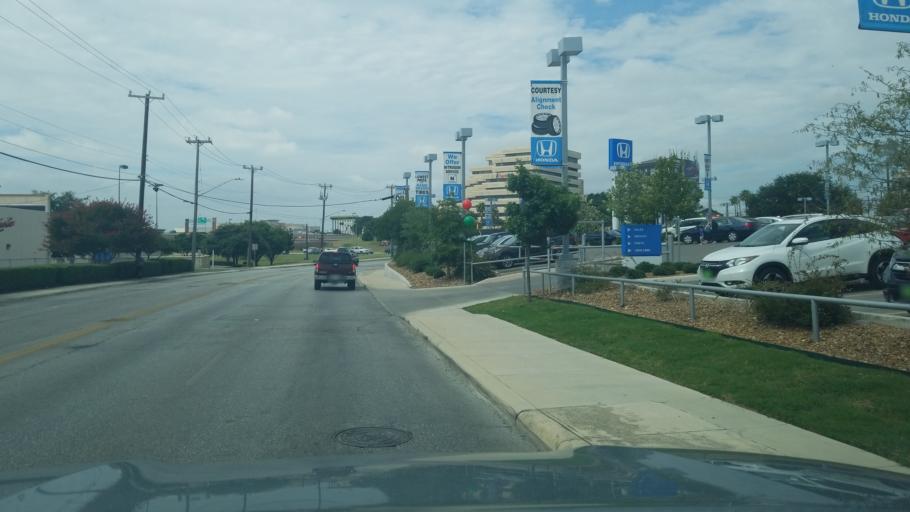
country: US
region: Texas
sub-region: Bexar County
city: Castle Hills
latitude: 29.5239
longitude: -98.4979
